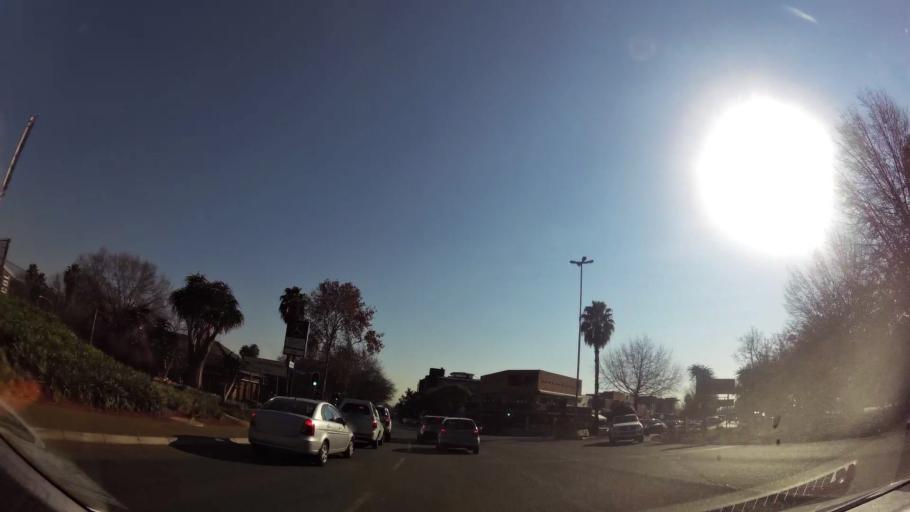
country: ZA
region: Gauteng
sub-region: Ekurhuleni Metropolitan Municipality
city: Germiston
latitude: -26.1800
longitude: 28.1362
